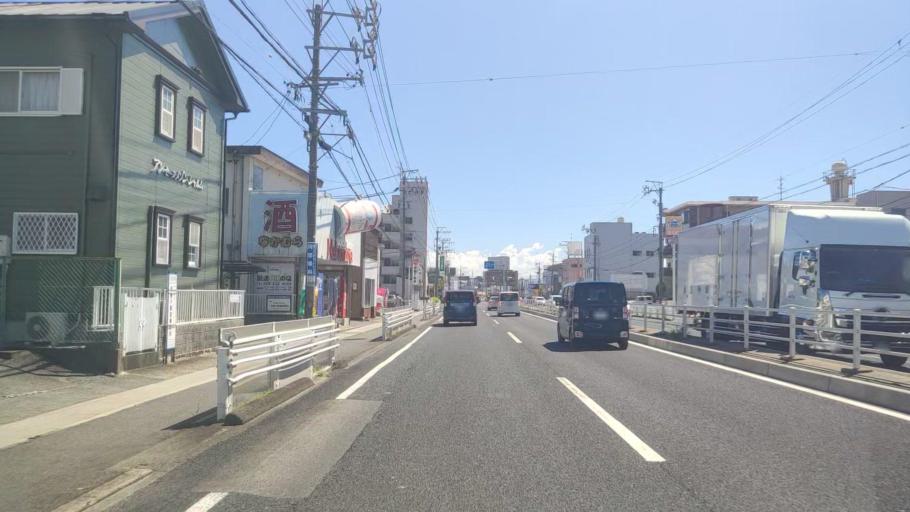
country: JP
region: Mie
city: Tsu-shi
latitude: 34.7456
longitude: 136.5196
